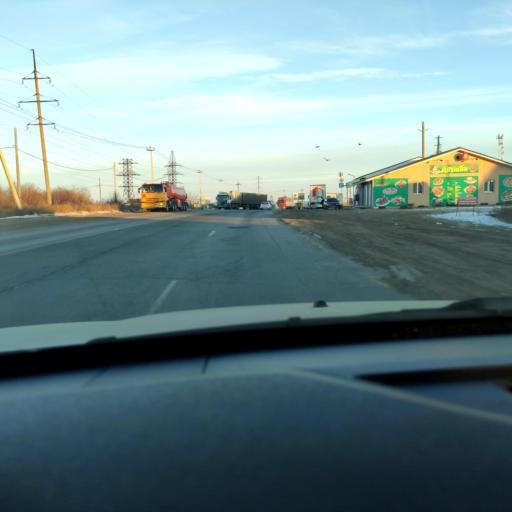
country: RU
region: Samara
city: Smyshlyayevka
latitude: 53.2479
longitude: 50.4747
